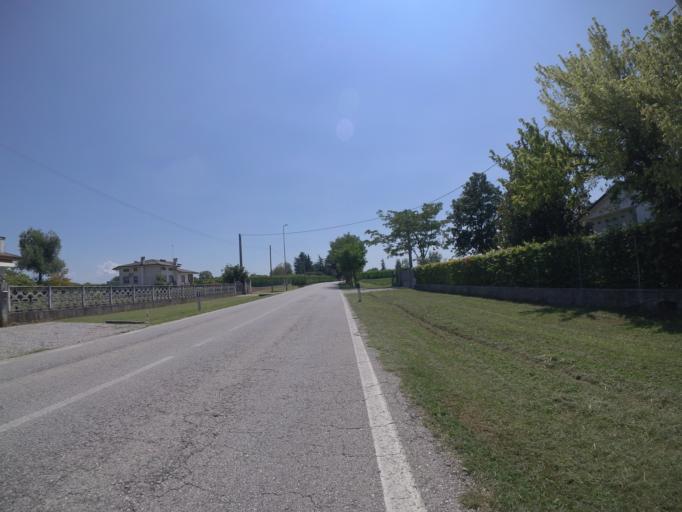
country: IT
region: Friuli Venezia Giulia
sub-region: Provincia di Udine
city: Lestizza
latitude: 45.9700
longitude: 13.1398
